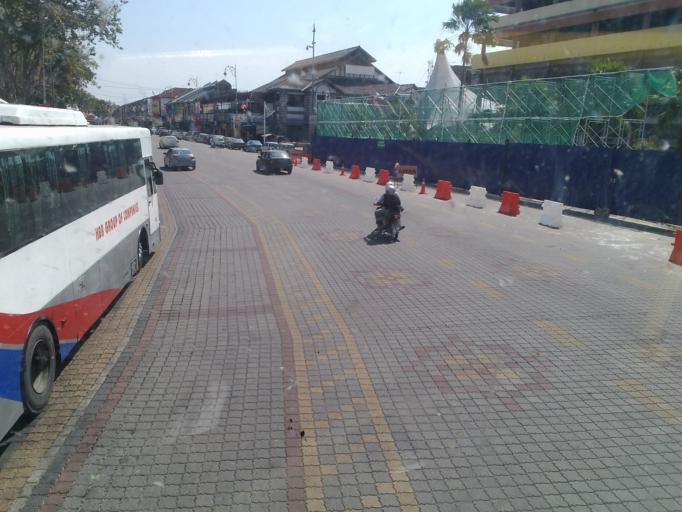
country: MY
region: Kedah
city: Alor Setar
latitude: 6.1174
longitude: 100.3671
